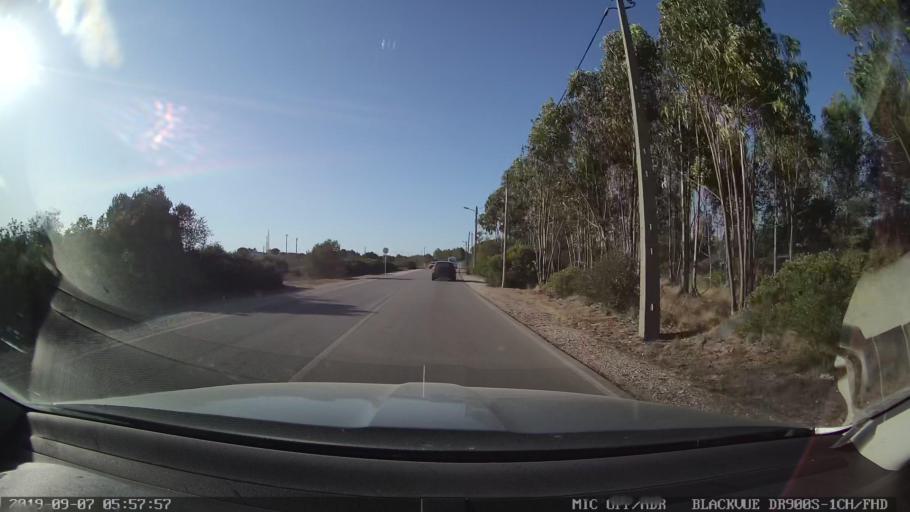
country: PT
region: Setubal
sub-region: Sesimbra
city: Sesimbra
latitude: 38.4553
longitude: -9.0925
